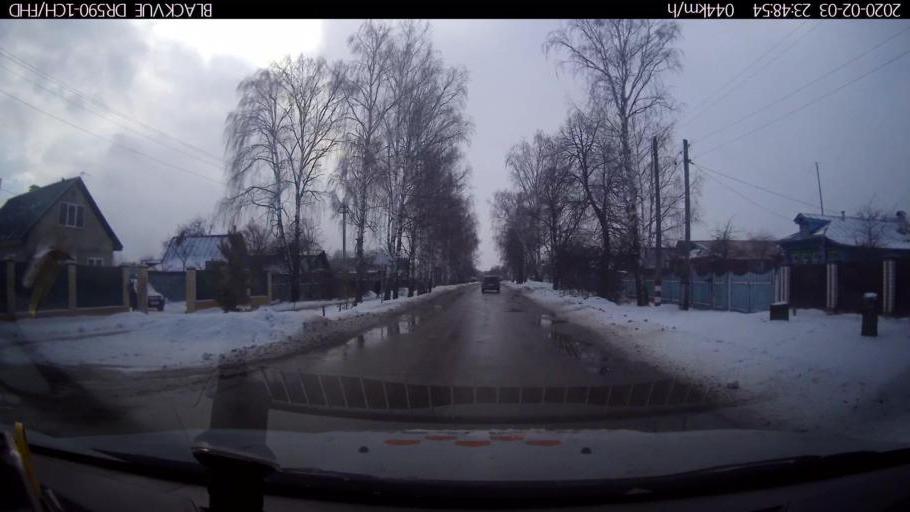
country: RU
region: Nizjnij Novgorod
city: Dal'neye Konstantinovo
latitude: 55.8105
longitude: 44.0908
